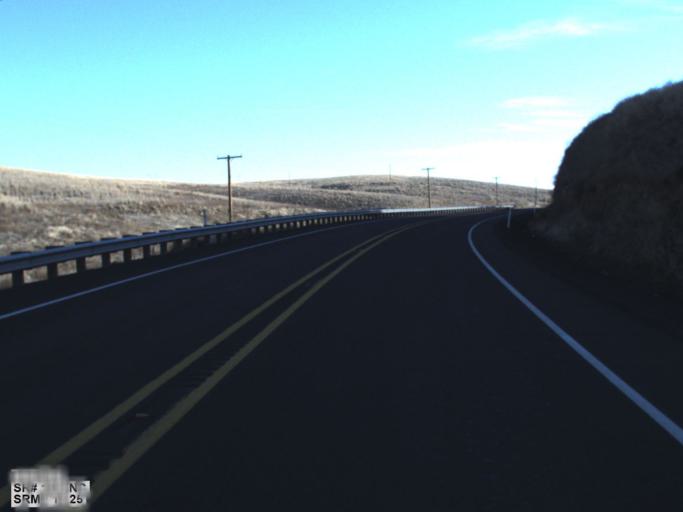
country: US
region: Washington
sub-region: Garfield County
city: Pomeroy
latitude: 46.6875
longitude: -117.8009
